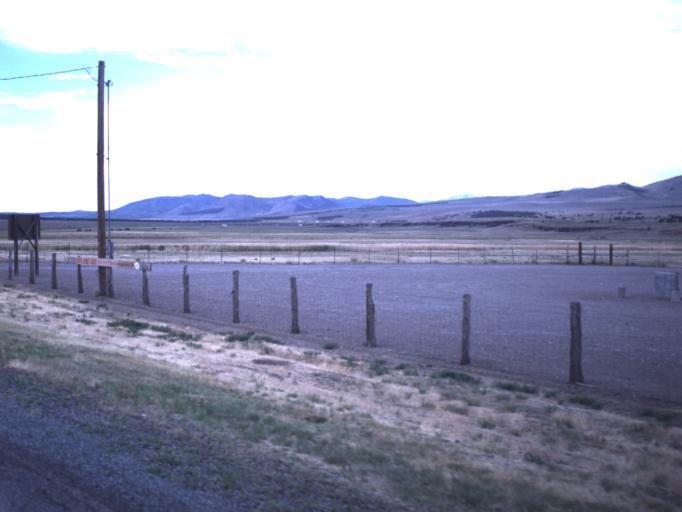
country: US
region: Utah
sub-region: Beaver County
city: Beaver
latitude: 38.5992
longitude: -112.5815
